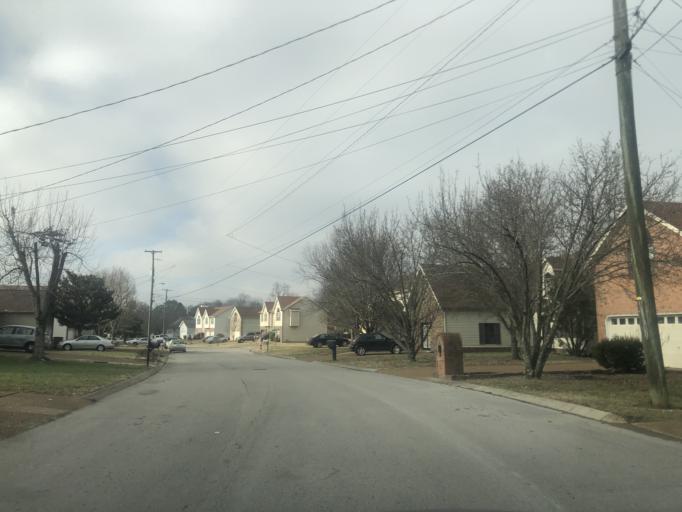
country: US
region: Tennessee
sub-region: Rutherford County
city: La Vergne
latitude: 36.0790
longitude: -86.6487
